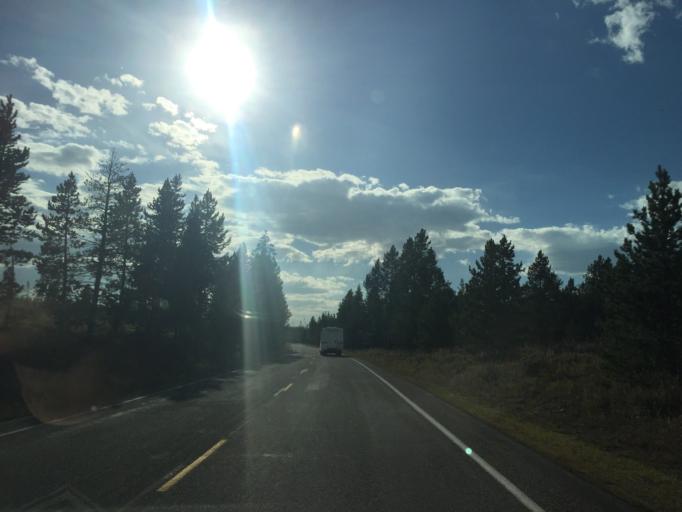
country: US
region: Montana
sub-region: Gallatin County
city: West Yellowstone
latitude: 44.6514
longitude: -111.0001
